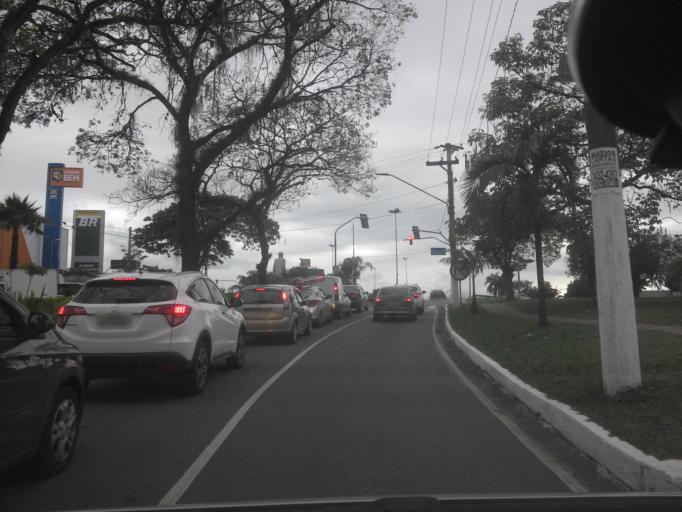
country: BR
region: Sao Paulo
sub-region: Taubate
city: Taubate
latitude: -23.0377
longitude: -45.5606
